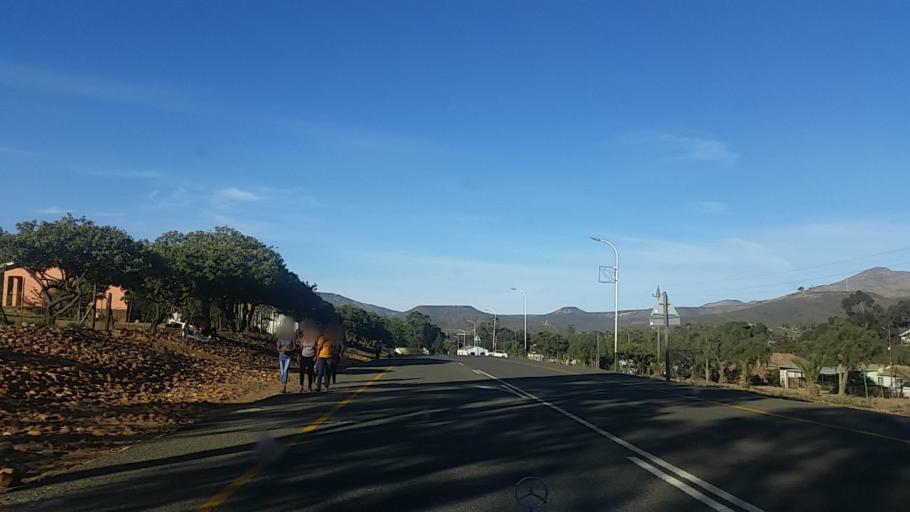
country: ZA
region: Western Cape
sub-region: Eden District Municipality
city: Knysna
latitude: -33.6608
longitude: 23.1135
